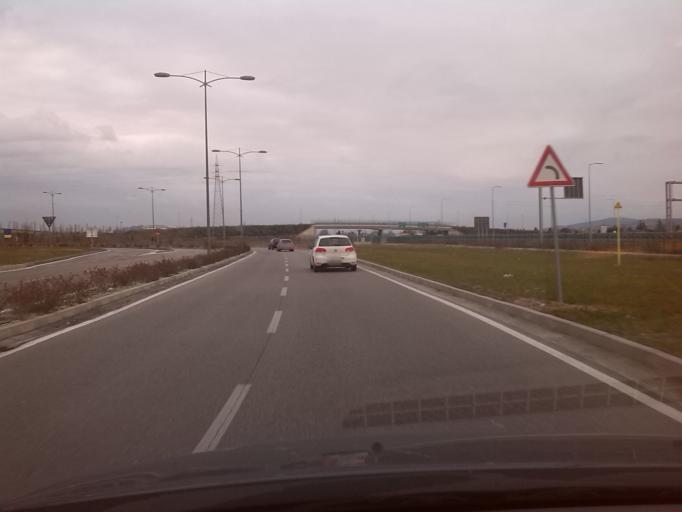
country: IT
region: Friuli Venezia Giulia
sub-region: Provincia di Gorizia
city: Villesse
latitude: 45.8648
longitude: 13.4340
